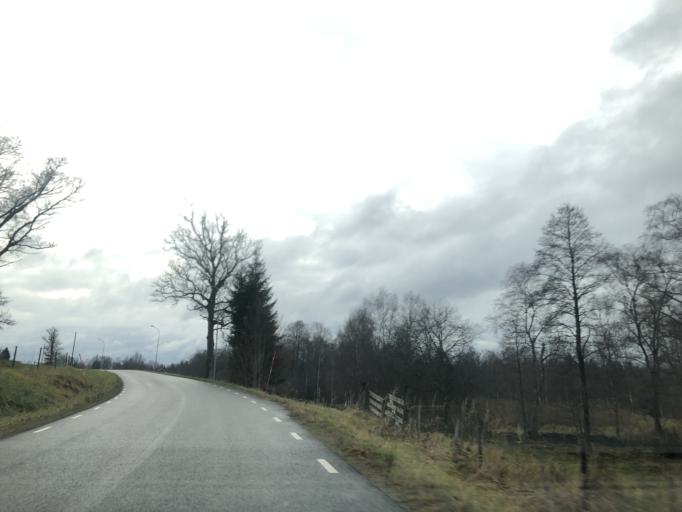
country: SE
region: Vaestra Goetaland
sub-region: Ulricehamns Kommun
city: Ulricehamn
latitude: 57.8195
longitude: 13.2456
